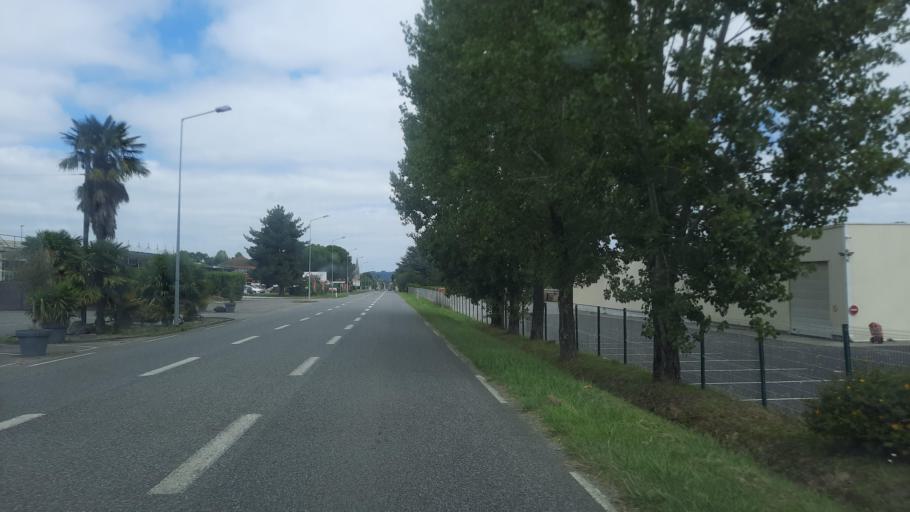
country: FR
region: Midi-Pyrenees
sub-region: Departement des Hautes-Pyrenees
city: Trie-sur-Baise
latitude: 43.3127
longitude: 0.3613
